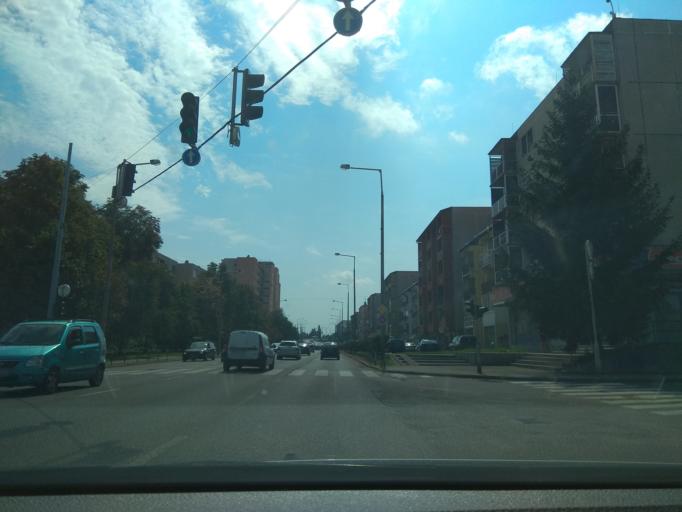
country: HU
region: Heves
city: Eger
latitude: 47.9142
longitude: 20.3699
